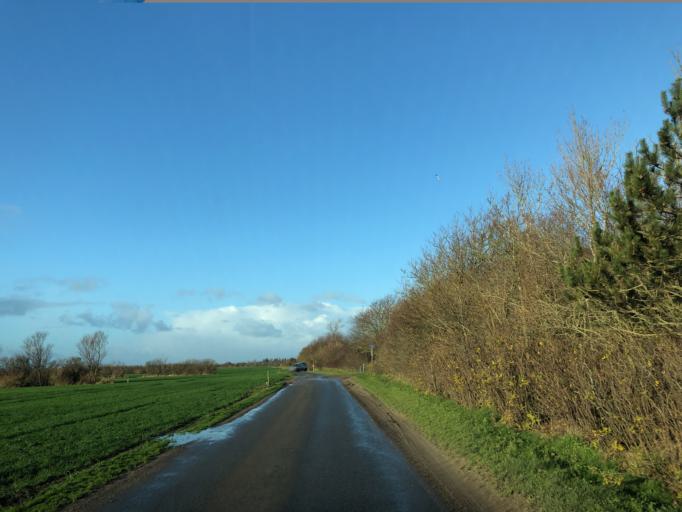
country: DK
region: Central Jutland
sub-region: Ringkobing-Skjern Kommune
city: Ringkobing
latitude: 56.1477
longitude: 8.2558
